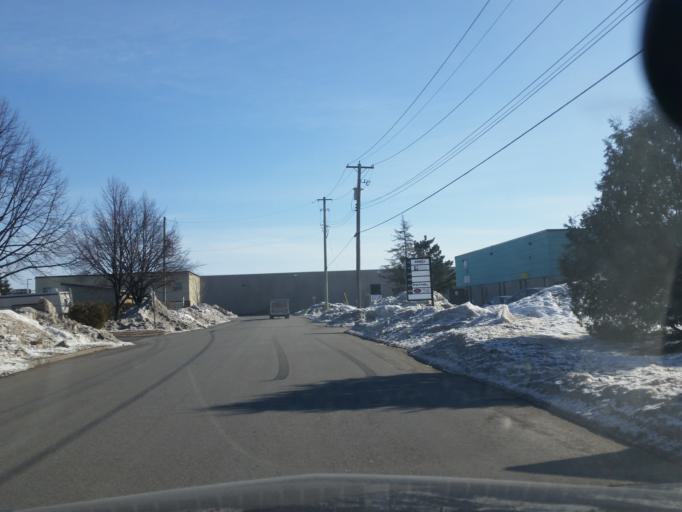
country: CA
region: Ontario
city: Ottawa
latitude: 45.3361
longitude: -75.7167
